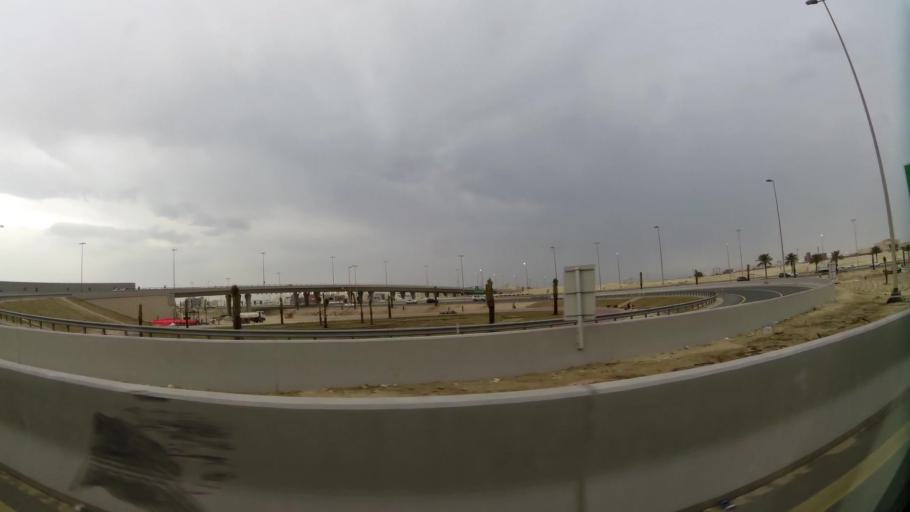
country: BH
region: Central Governorate
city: Dar Kulayb
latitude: 26.0828
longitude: 50.5167
